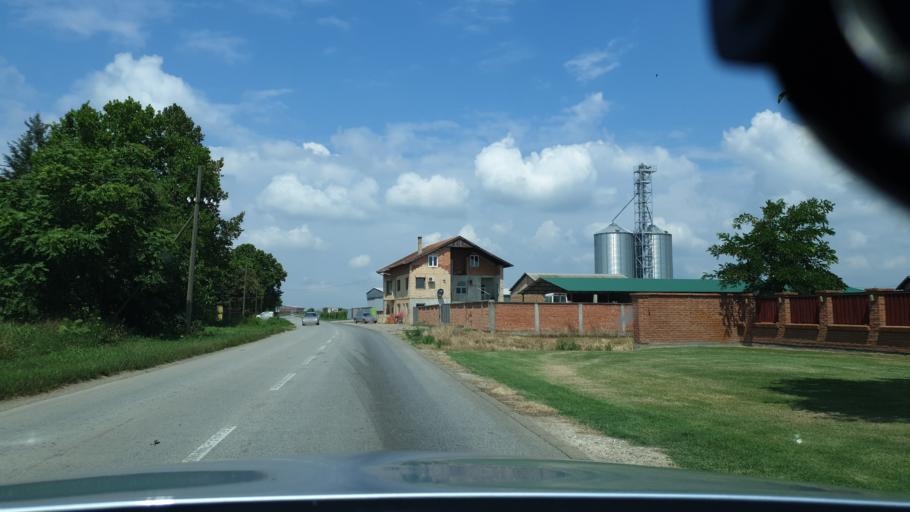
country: RS
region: Autonomna Pokrajina Vojvodina
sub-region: Juznobacki Okrug
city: Kovilj
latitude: 45.2412
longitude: 20.0254
